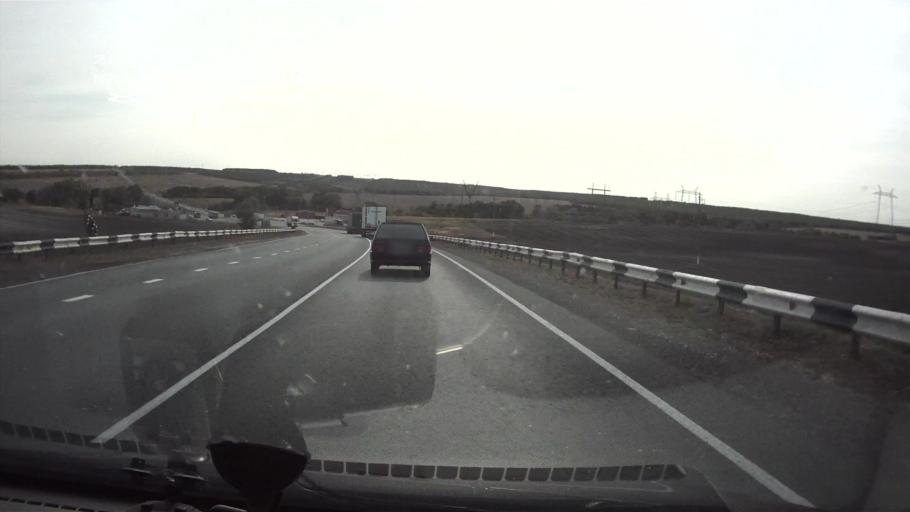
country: RU
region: Saratov
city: Sinodskoye
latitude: 51.9255
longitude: 46.5665
